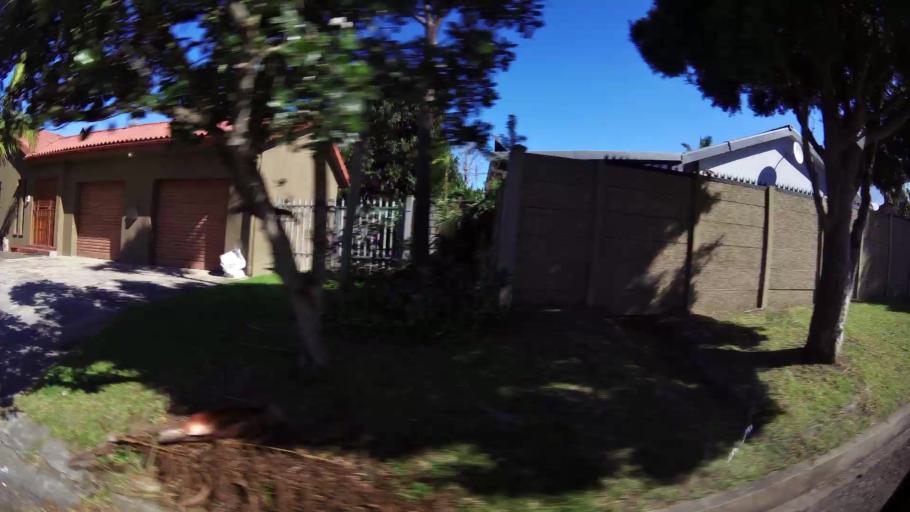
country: ZA
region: Western Cape
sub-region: Eden District Municipality
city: George
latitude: -33.9475
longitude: 22.4792
